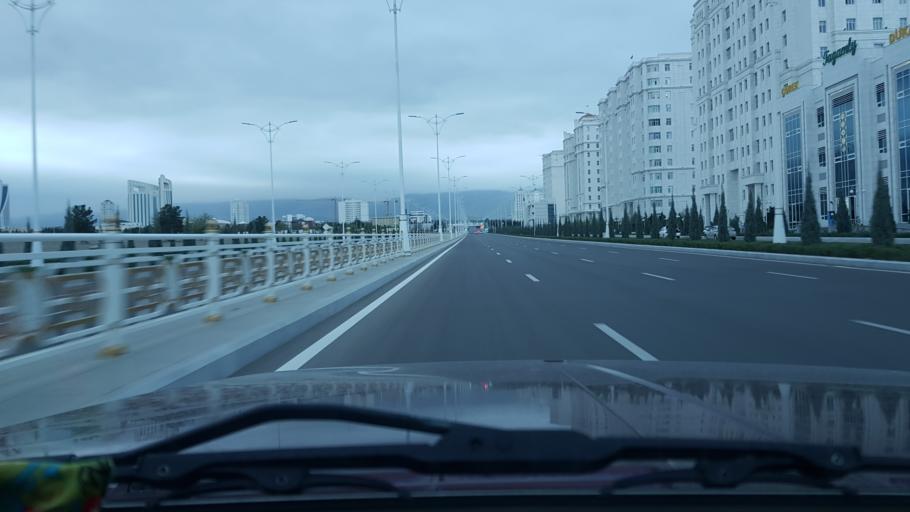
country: TM
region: Ahal
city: Ashgabat
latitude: 37.8905
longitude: 58.3647
